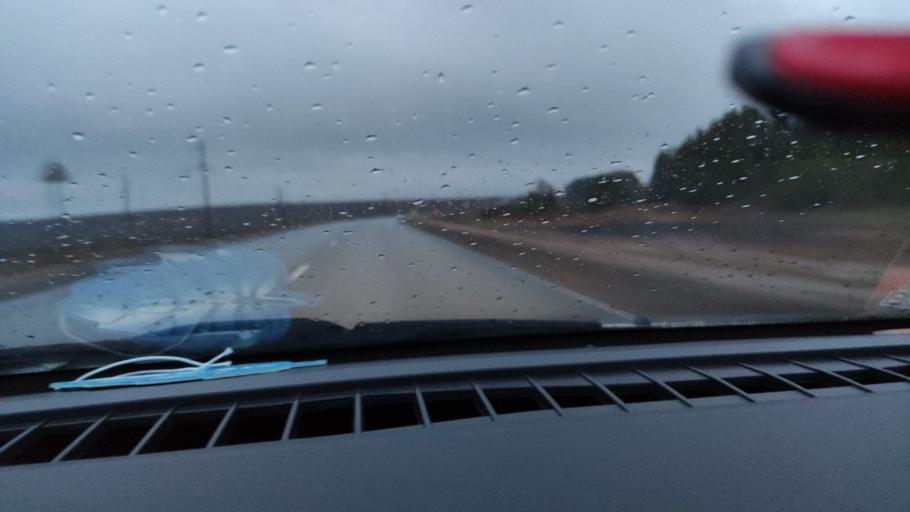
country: RU
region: Udmurtiya
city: Alnashi
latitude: 56.2941
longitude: 52.3507
